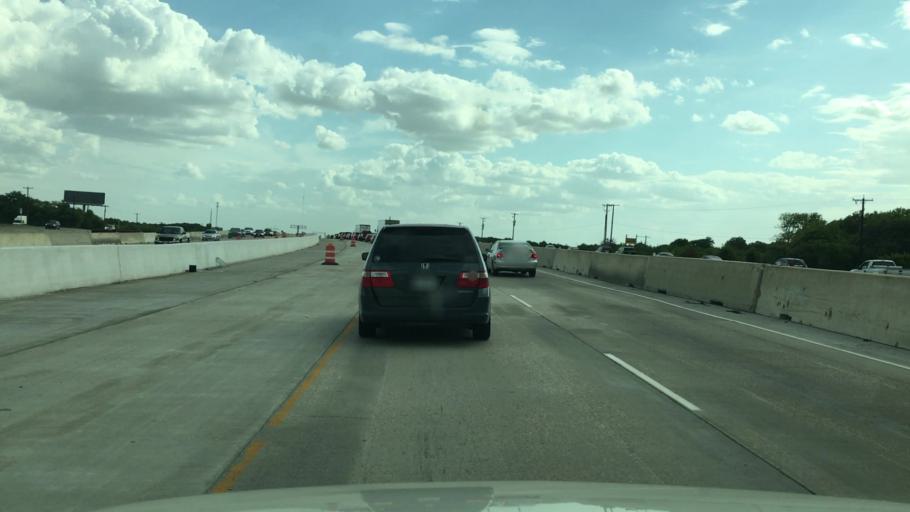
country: US
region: Texas
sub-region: McLennan County
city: Bruceville-Eddy
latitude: 31.3177
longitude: -97.2384
